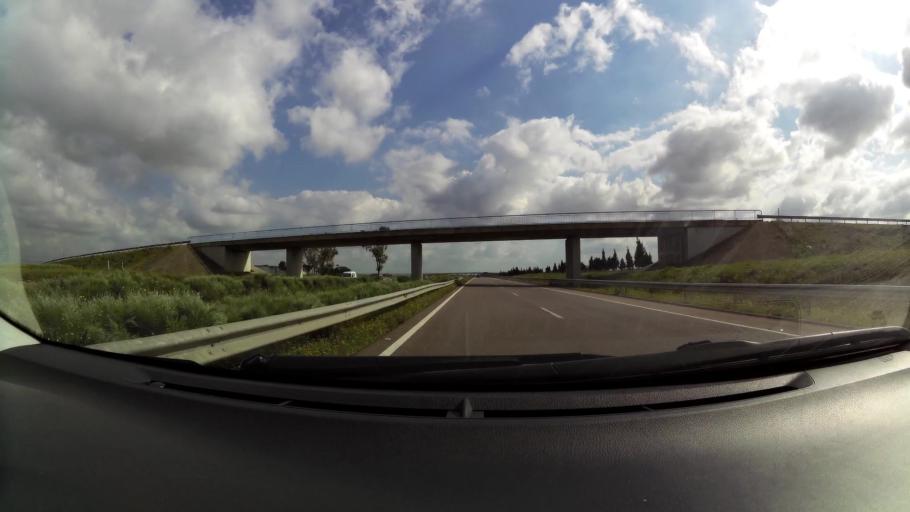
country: MA
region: Chaouia-Ouardigha
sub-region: Settat Province
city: Berrechid
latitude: 33.2046
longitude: -7.5756
